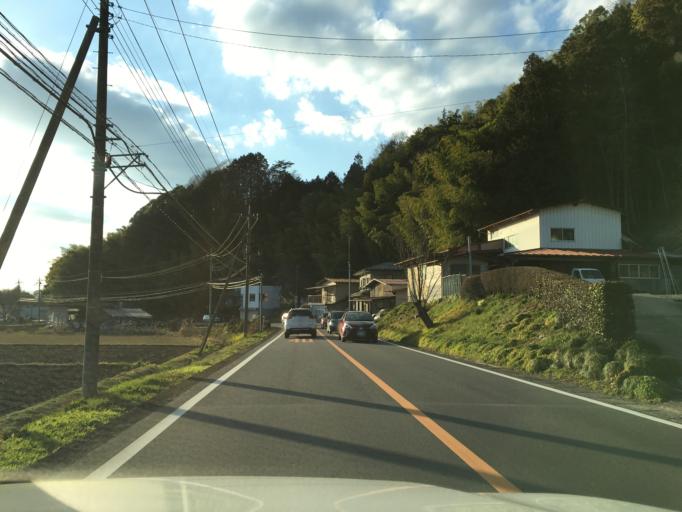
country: JP
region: Tochigi
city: Otawara
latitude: 36.8703
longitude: 140.1495
